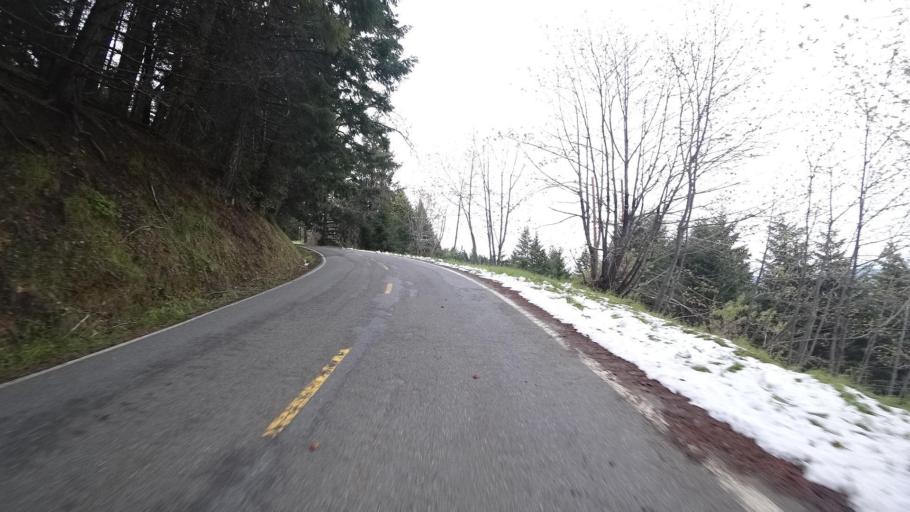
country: US
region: California
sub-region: Humboldt County
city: Willow Creek
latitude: 40.8870
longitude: -123.7714
